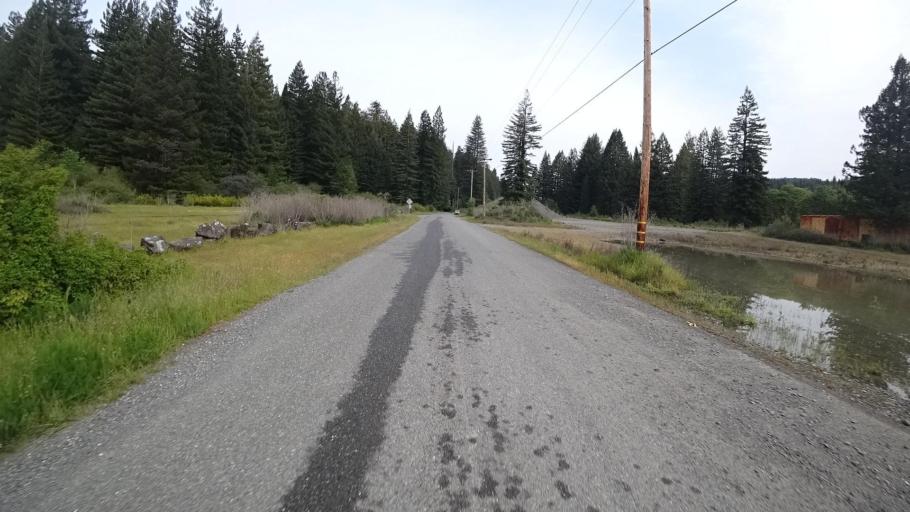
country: US
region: California
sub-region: Humboldt County
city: Redway
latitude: 40.3452
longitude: -123.9170
